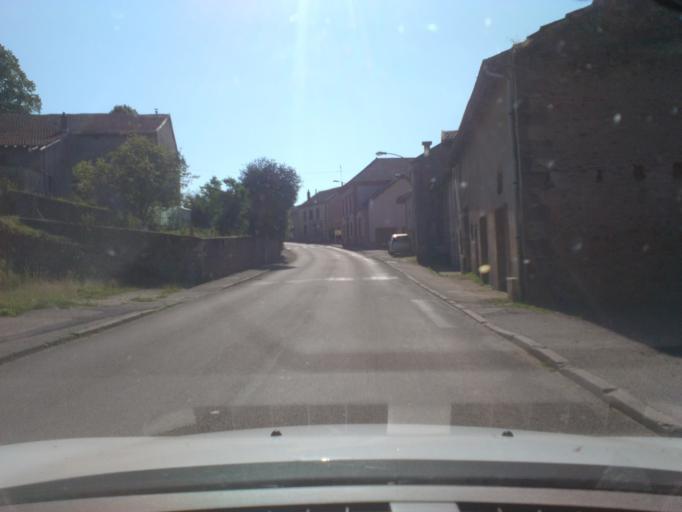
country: FR
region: Lorraine
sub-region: Departement des Vosges
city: Bruyeres
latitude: 48.2391
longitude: 6.6659
